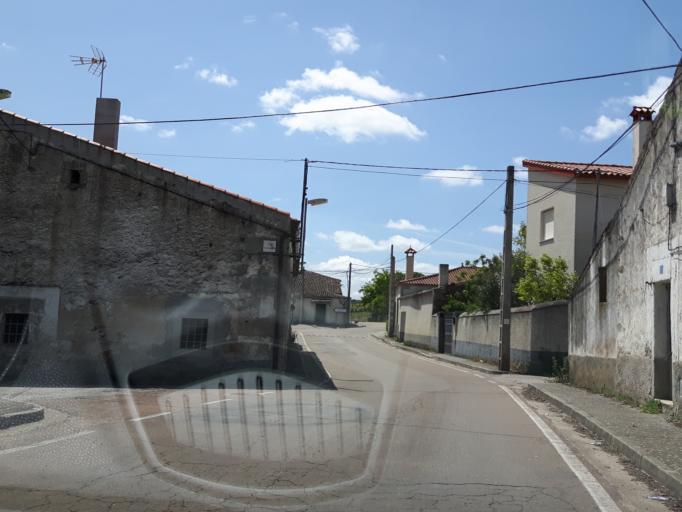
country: ES
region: Castille and Leon
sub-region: Provincia de Salamanca
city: Aldea del Obispo
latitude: 40.7072
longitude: -6.7947
